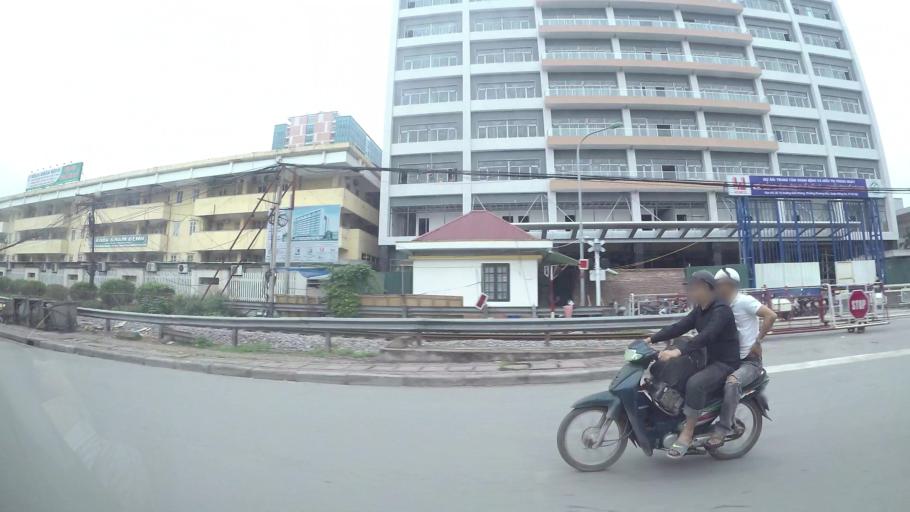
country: VN
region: Ha Noi
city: Hai BaTrung
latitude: 21.0033
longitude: 105.8413
